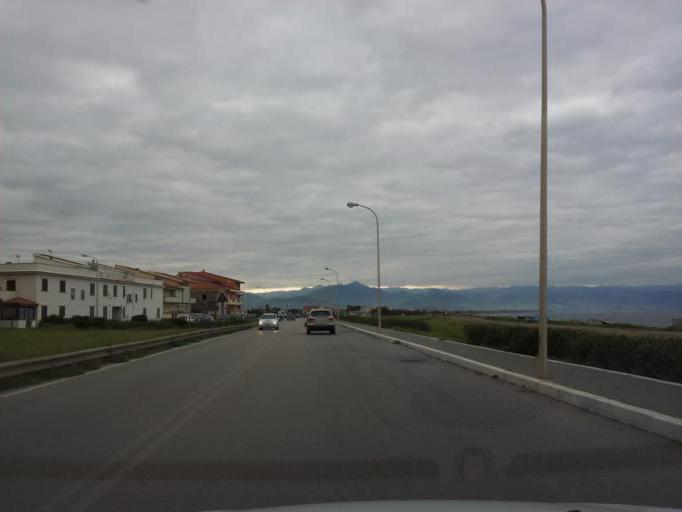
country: IT
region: Sicily
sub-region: Messina
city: Milazzo
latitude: 38.2081
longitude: 15.2282
